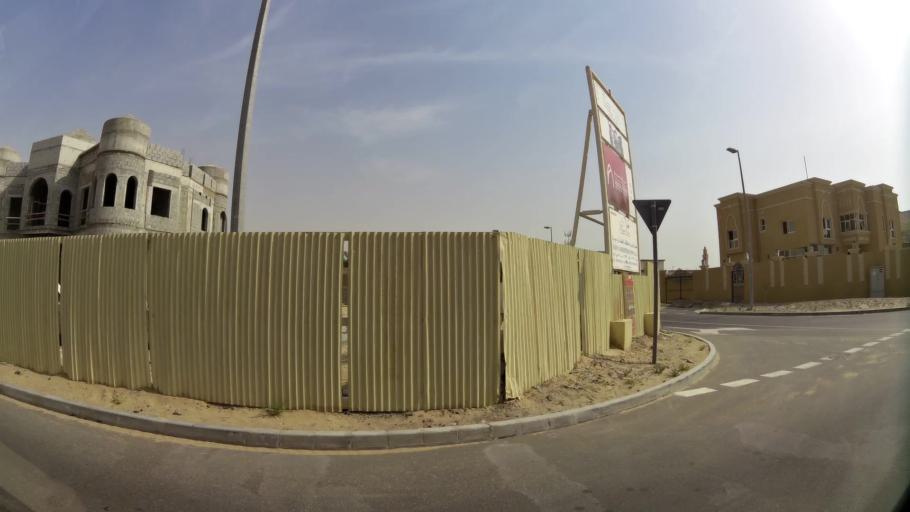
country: AE
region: Ash Shariqah
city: Sharjah
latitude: 25.2623
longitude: 55.4606
